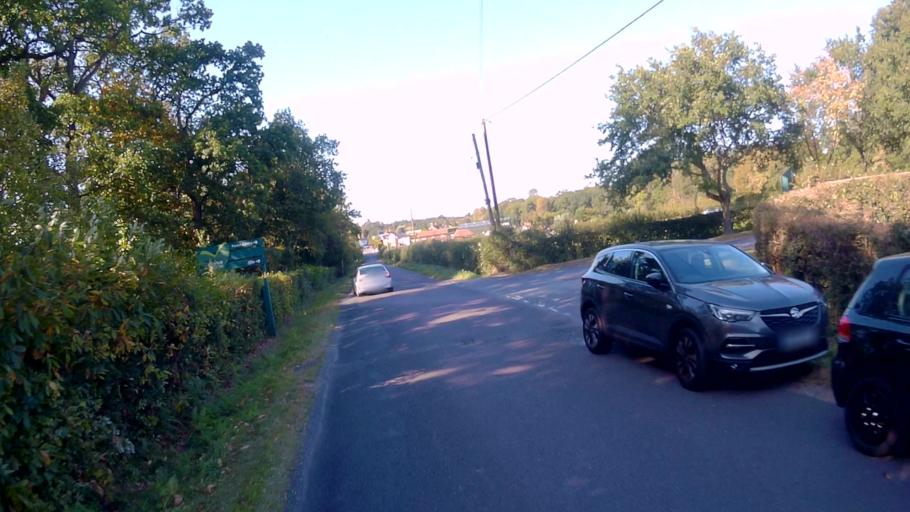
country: GB
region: England
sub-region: Hampshire
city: Kingsley
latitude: 51.1668
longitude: -0.8453
